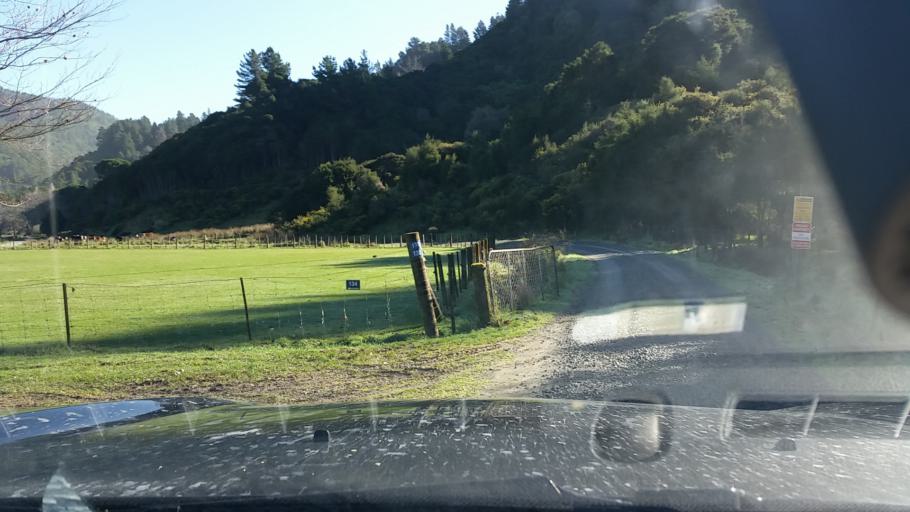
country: NZ
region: Marlborough
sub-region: Marlborough District
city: Blenheim
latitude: -41.4587
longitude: 173.7854
